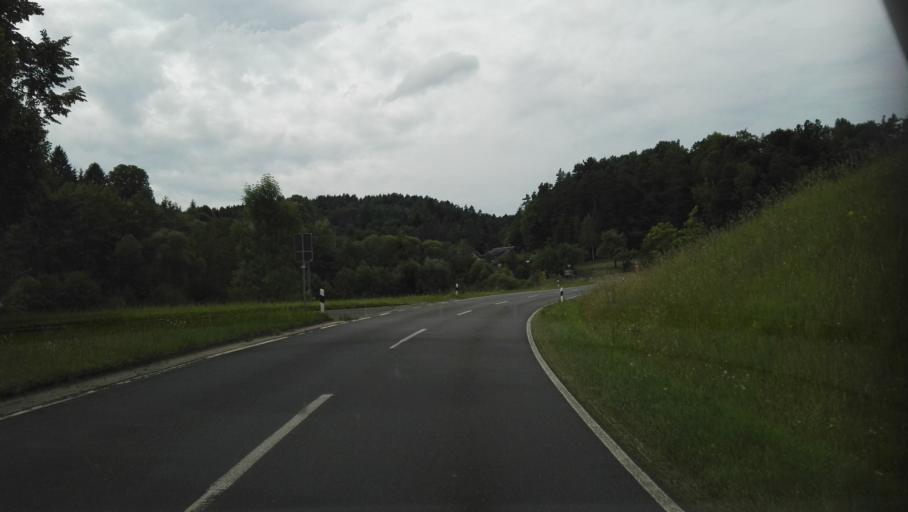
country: DE
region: Bavaria
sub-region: Upper Franconia
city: Plankenfels
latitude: 49.8779
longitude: 11.3363
